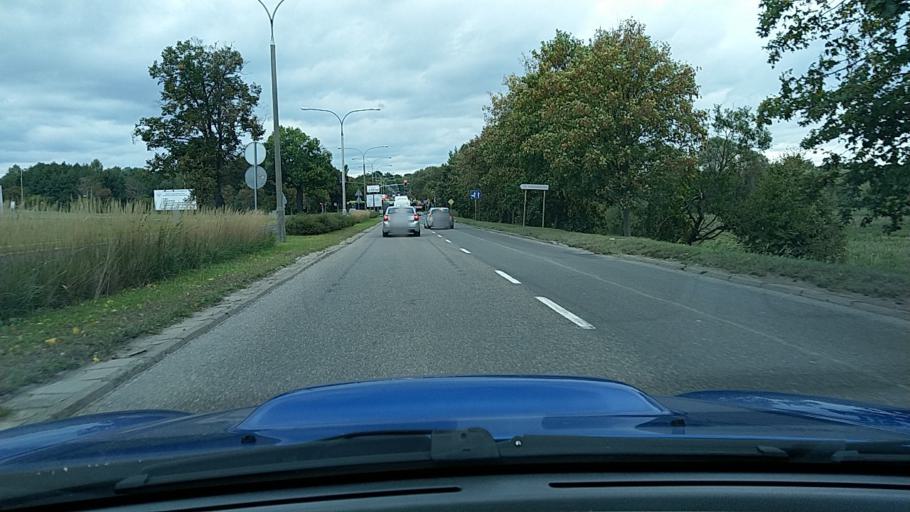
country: PL
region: Warmian-Masurian Voivodeship
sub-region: Olsztyn
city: Kortowo
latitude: 53.7507
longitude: 20.4610
